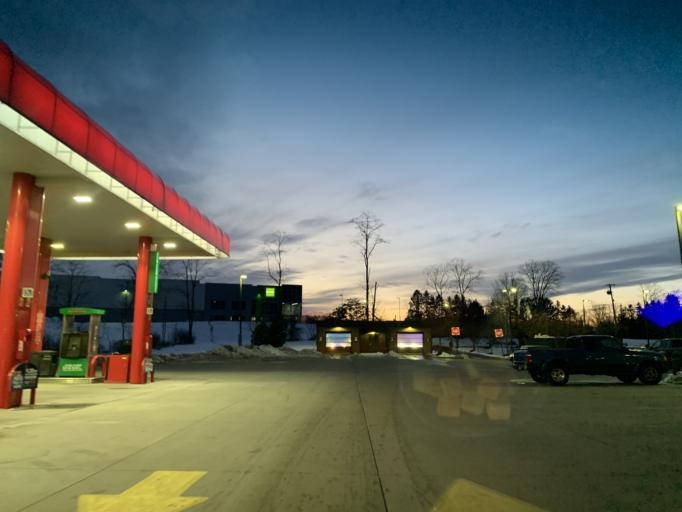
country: US
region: Pennsylvania
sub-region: Cumberland County
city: Carlisle
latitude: 40.1901
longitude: -77.2414
